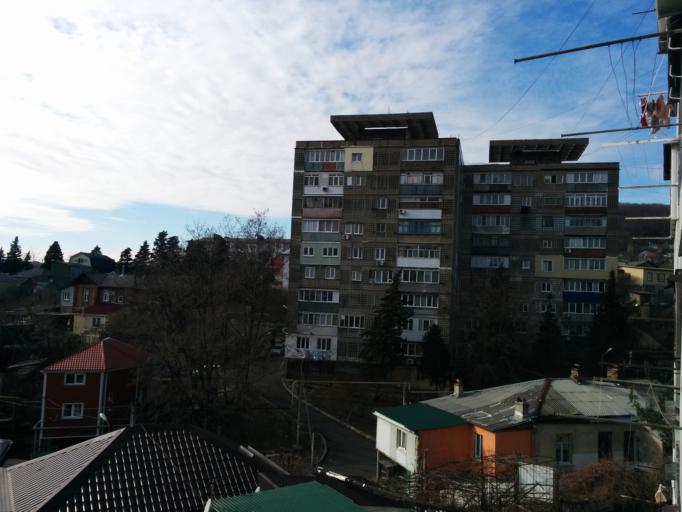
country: RU
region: Krasnodarskiy
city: Tuapse
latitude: 44.1031
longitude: 39.0849
